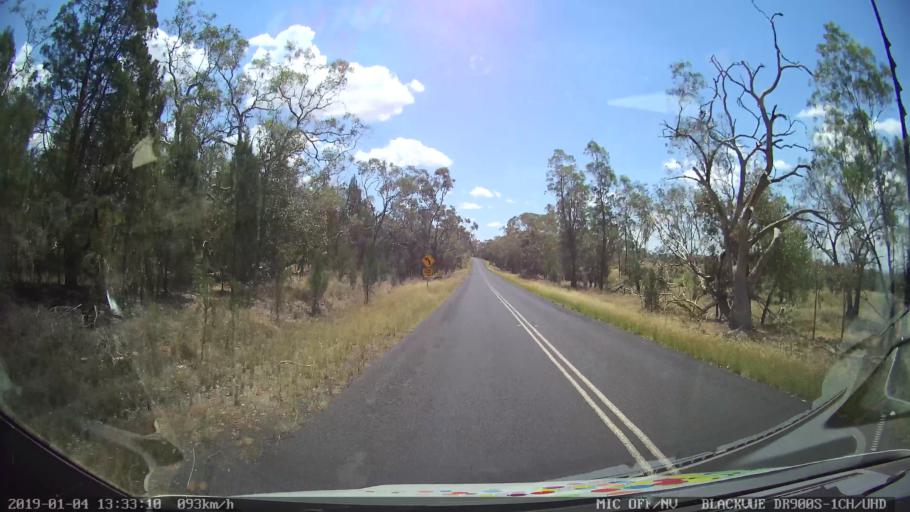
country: AU
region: New South Wales
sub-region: Dubbo Municipality
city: Eulomogo
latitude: -32.6007
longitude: 148.5445
